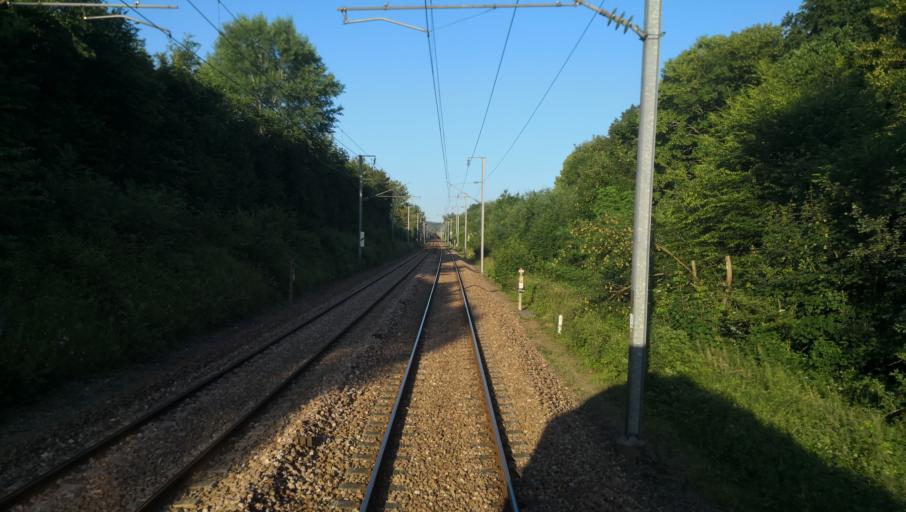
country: FR
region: Lower Normandy
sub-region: Departement du Calvados
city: Beuvillers
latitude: 49.1225
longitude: 0.3140
